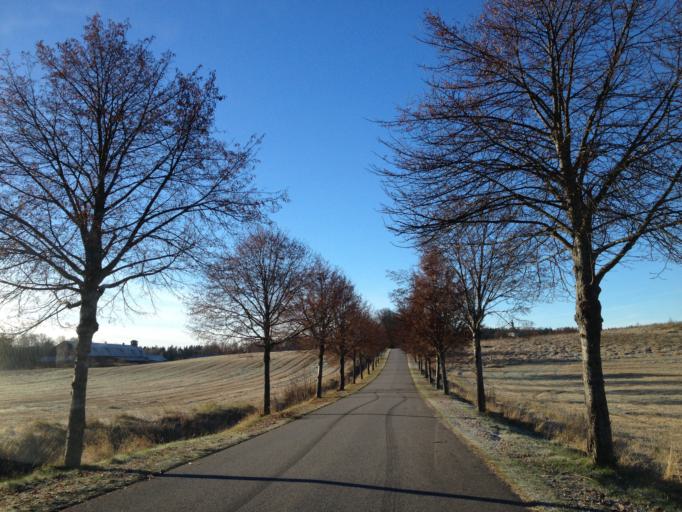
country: SE
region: Stockholm
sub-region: Sodertalje Kommun
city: Soedertaelje
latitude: 59.1607
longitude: 17.6108
